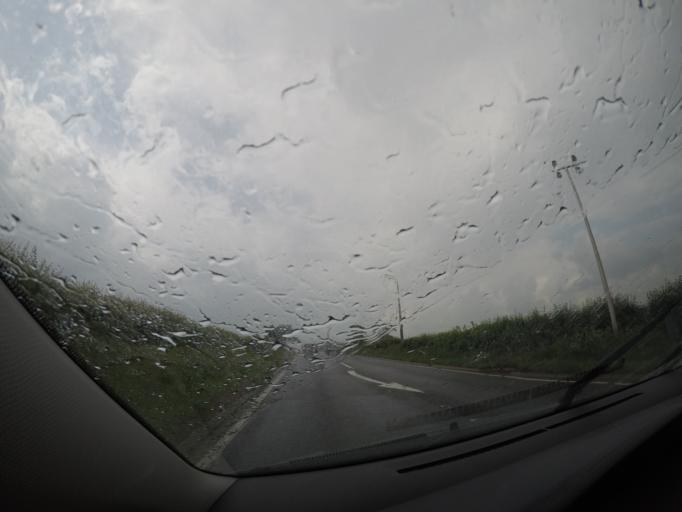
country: GB
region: England
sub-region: Cumbria
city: Appleby-in-Westmorland
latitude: 54.6246
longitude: -2.5729
